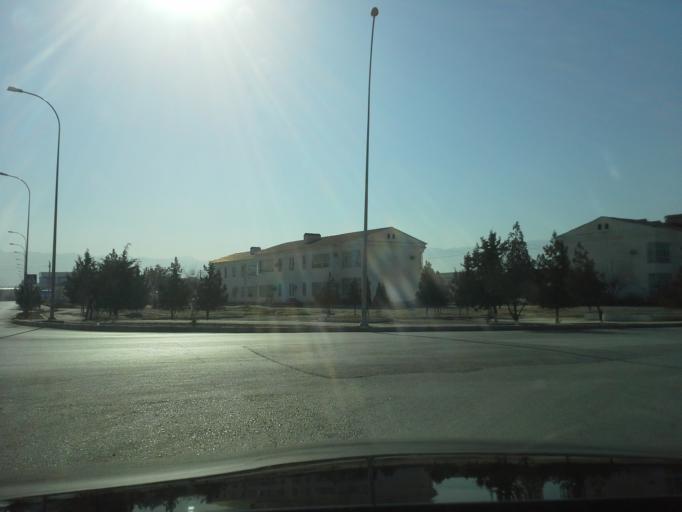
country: TM
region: Ahal
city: Annau
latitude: 37.9058
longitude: 58.4984
